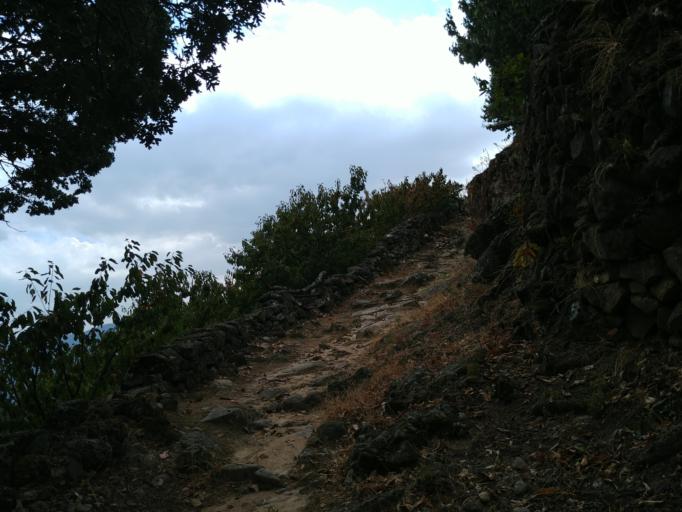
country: ES
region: Extremadura
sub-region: Provincia de Caceres
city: Cabezabellosa
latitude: 40.1371
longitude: -5.9526
